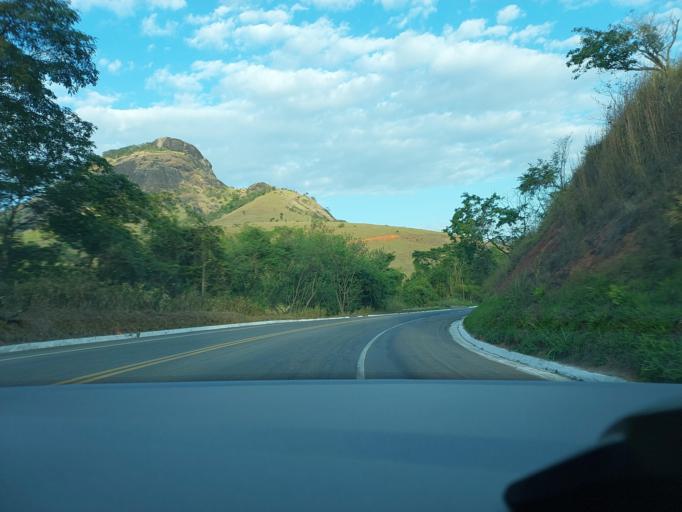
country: BR
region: Minas Gerais
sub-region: Muriae
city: Muriae
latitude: -21.1294
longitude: -42.3187
